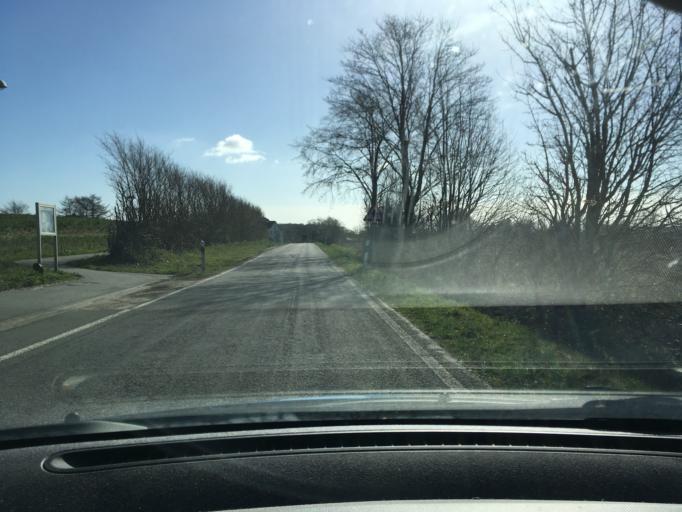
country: DE
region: Schleswig-Holstein
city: Borgwedel
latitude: 54.4945
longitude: 9.6553
